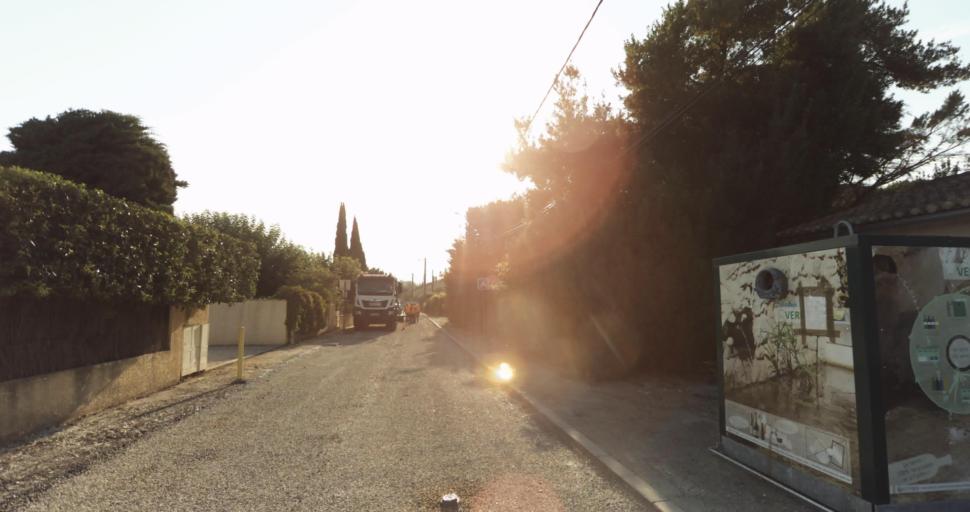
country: FR
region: Provence-Alpes-Cote d'Azur
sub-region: Departement du Vaucluse
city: Monteux
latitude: 44.0398
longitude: 5.0008
